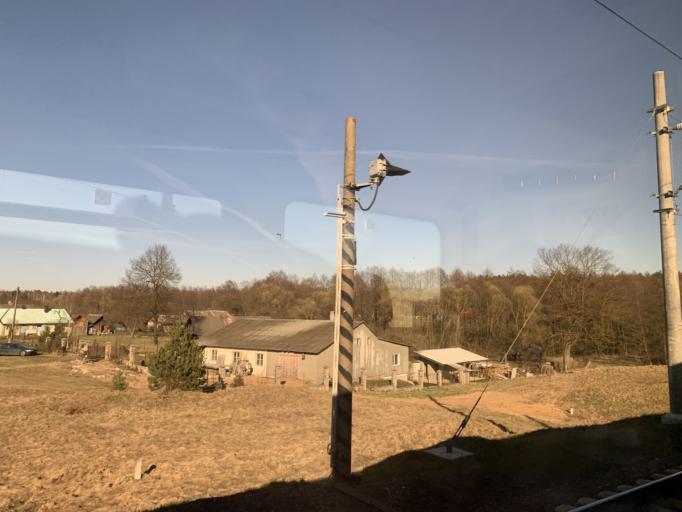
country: BY
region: Grodnenskaya
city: Smarhon'
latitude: 54.4323
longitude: 26.5215
